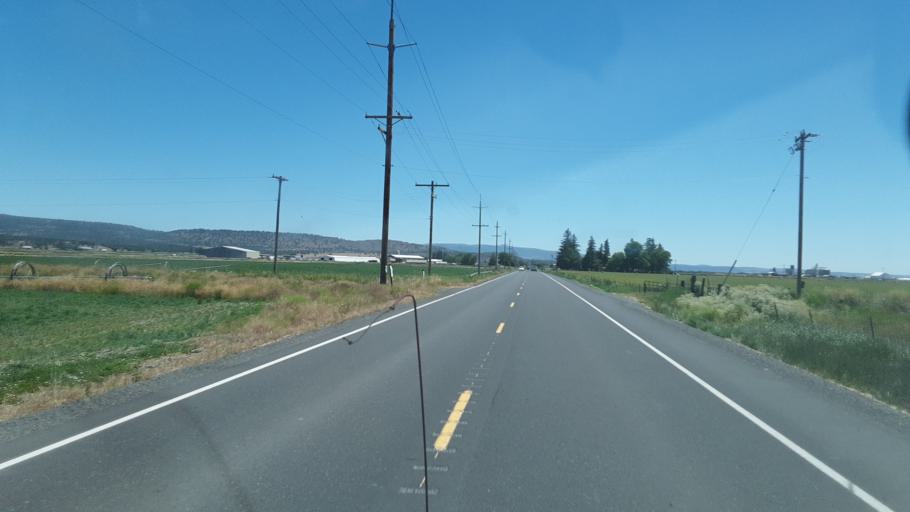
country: US
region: California
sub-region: Siskiyou County
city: Tulelake
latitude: 42.0240
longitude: -121.5814
